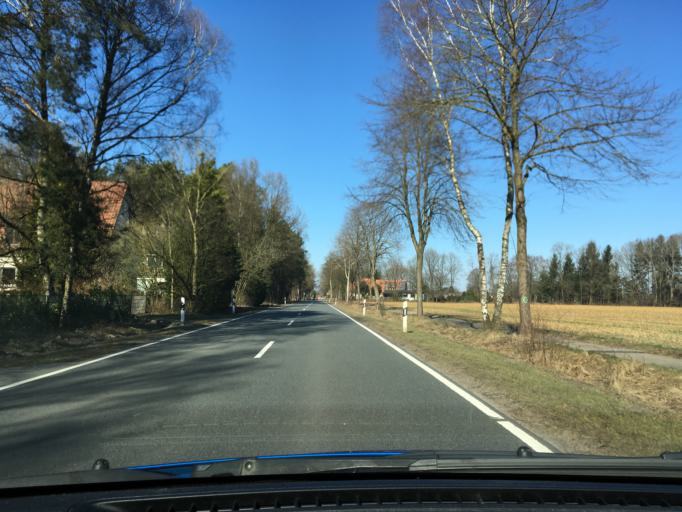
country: DE
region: Lower Saxony
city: Schneverdingen
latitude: 53.0795
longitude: 9.8101
